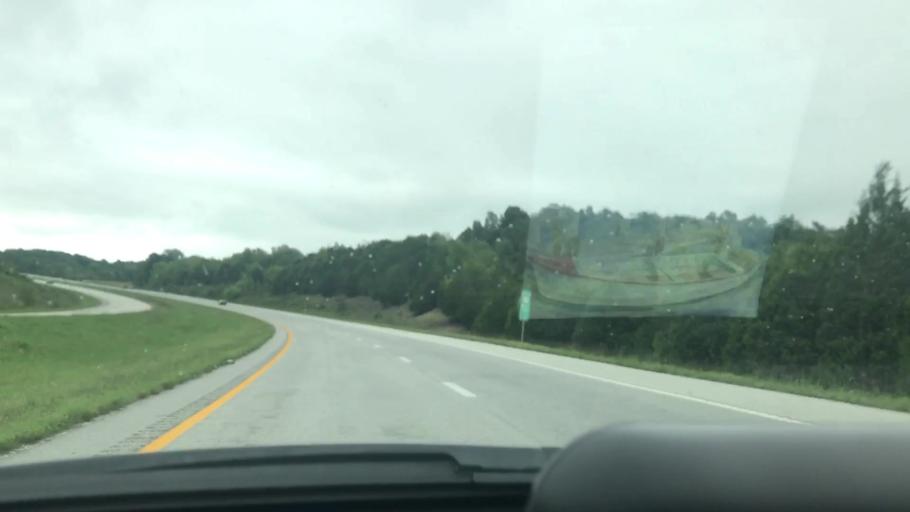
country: US
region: Missouri
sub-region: Greene County
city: Strafford
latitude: 37.2900
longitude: -93.1830
